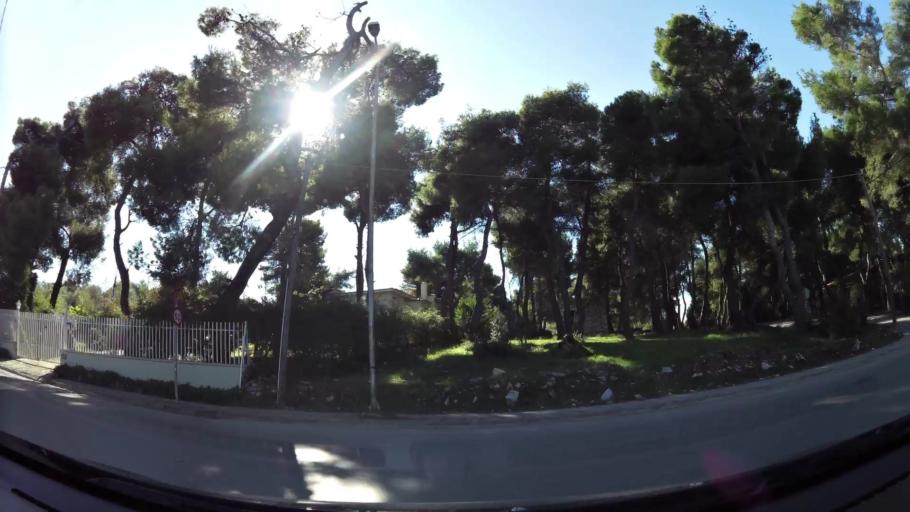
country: GR
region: Attica
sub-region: Nomarchia Anatolikis Attikis
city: Drosia
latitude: 38.1194
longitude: 23.8716
